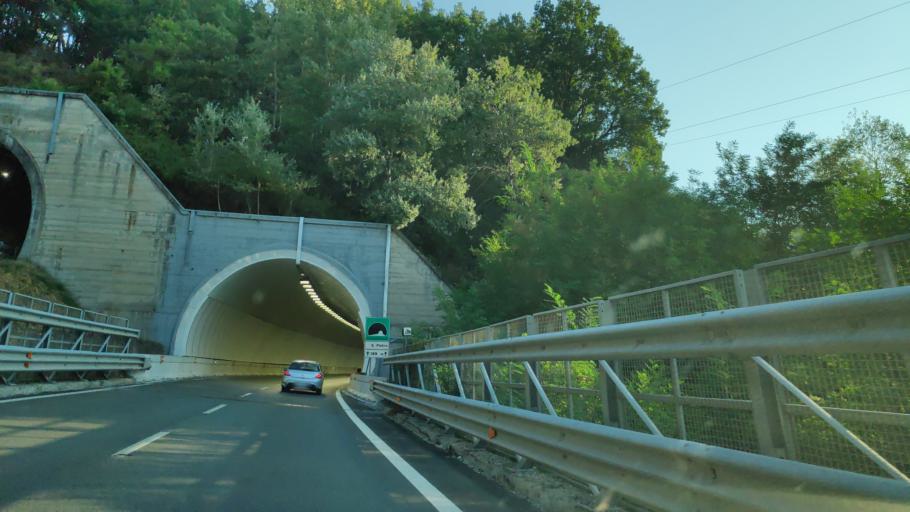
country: IT
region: Calabria
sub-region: Provincia di Cosenza
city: Belsito
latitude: 39.1750
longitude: 16.2940
